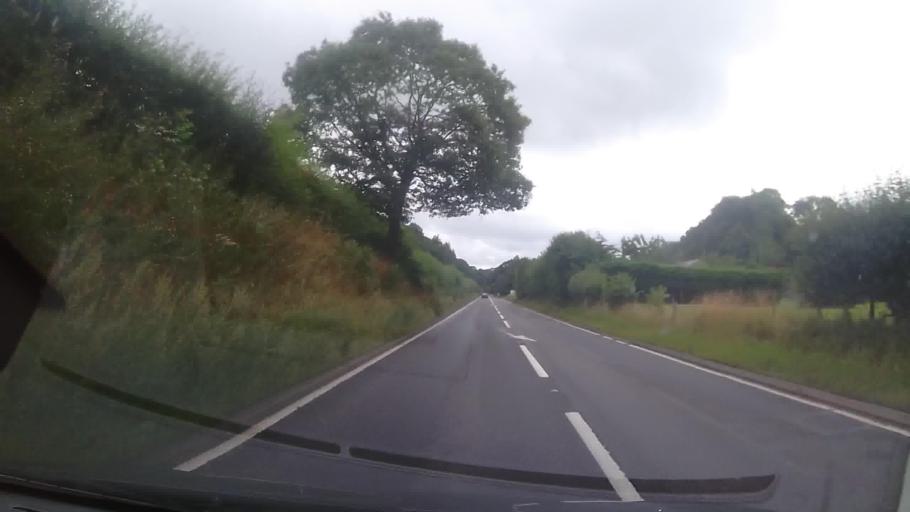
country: GB
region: England
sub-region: Shropshire
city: Church Stretton
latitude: 52.5140
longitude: -2.8243
